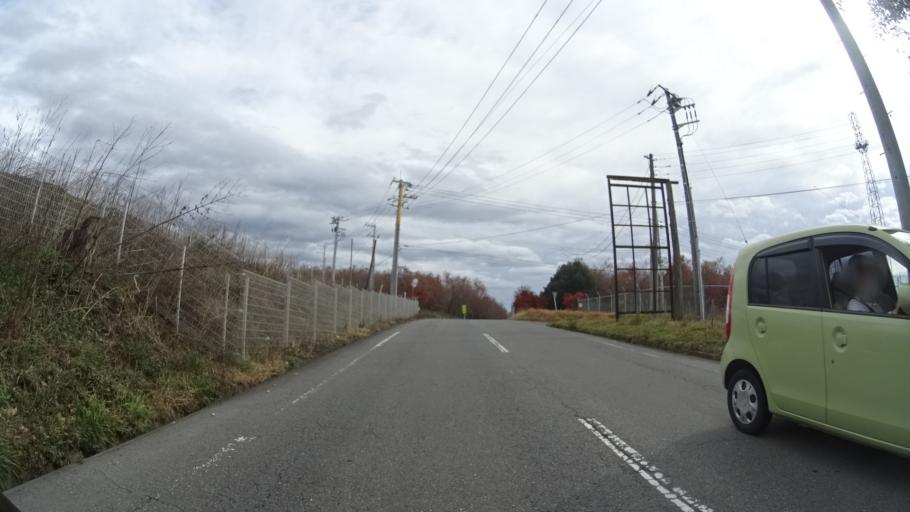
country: JP
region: Gunma
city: Maebashi-shi
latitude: 36.4757
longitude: 139.1293
